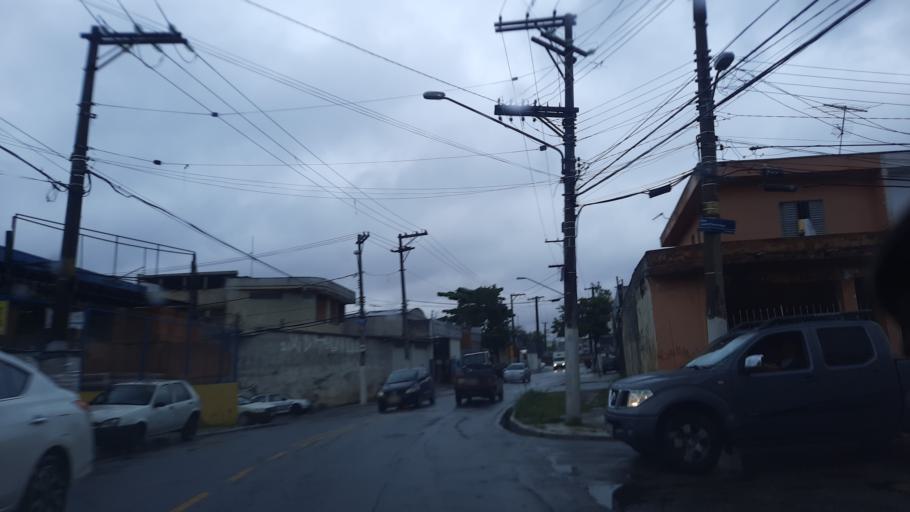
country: BR
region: Sao Paulo
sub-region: Guarulhos
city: Guarulhos
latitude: -23.4661
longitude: -46.5702
